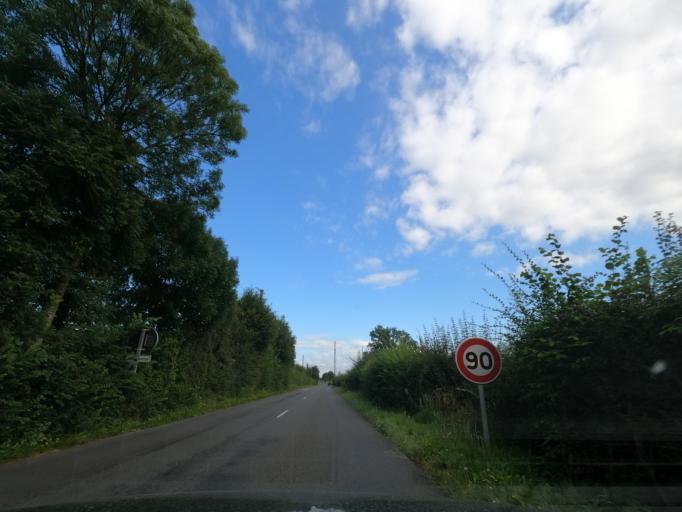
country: FR
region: Lower Normandy
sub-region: Departement de l'Orne
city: Gace
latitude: 48.7588
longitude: 0.1877
